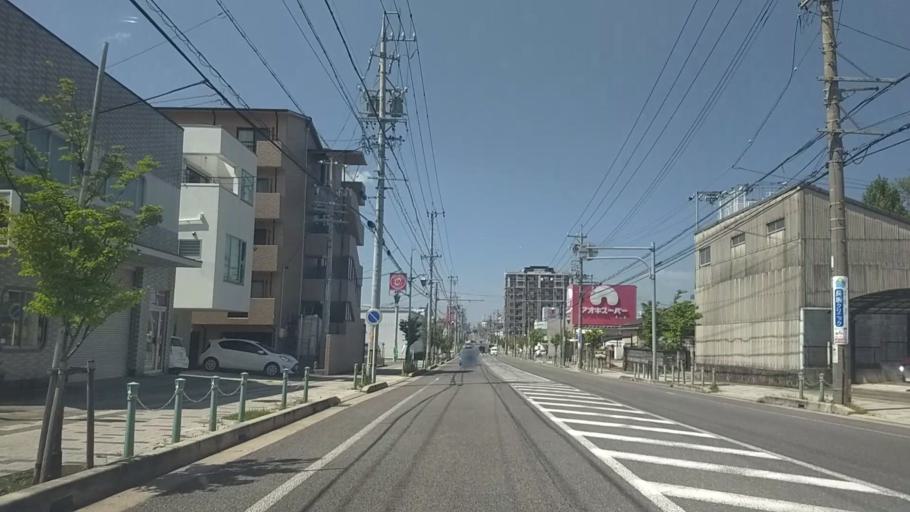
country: JP
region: Aichi
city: Okazaki
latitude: 34.9677
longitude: 137.1716
